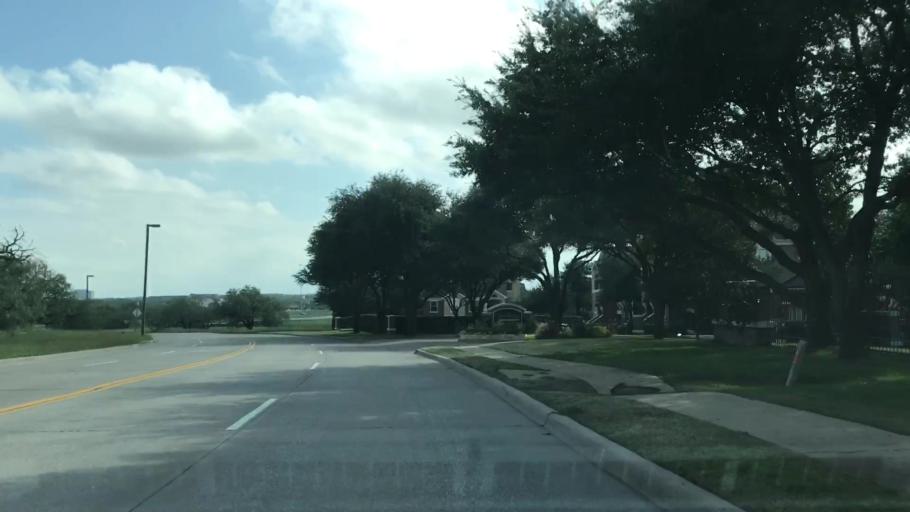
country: US
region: Texas
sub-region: Dallas County
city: Farmers Branch
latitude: 32.8932
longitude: -96.9555
